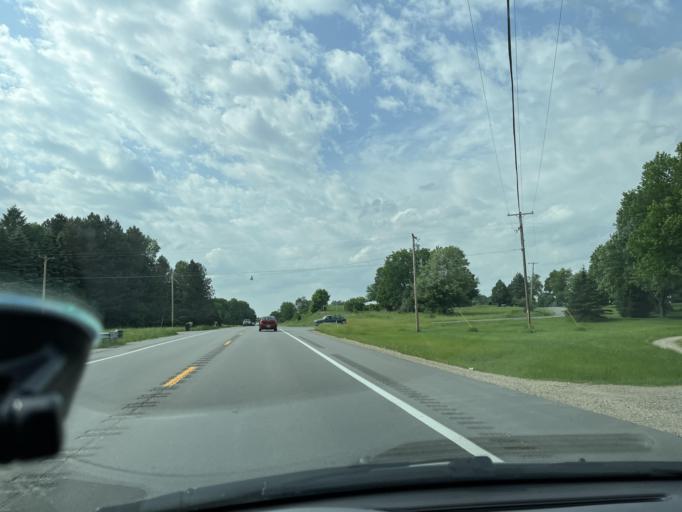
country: US
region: Michigan
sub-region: Barry County
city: Middleville
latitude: 42.7326
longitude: -85.4816
